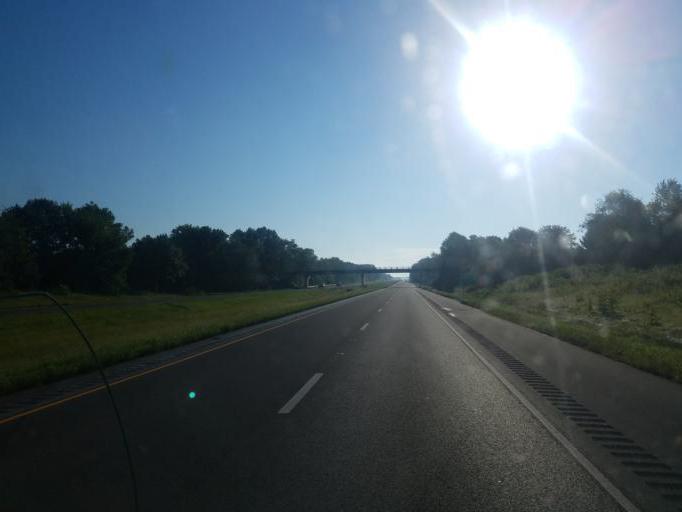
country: US
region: Illinois
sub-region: Fayette County
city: Vandalia
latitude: 38.9789
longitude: -88.9670
